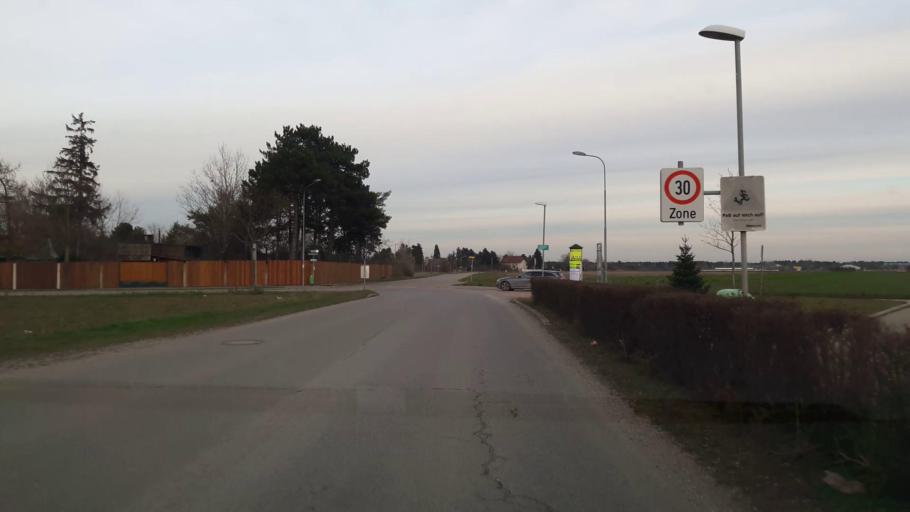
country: AT
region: Lower Austria
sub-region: Politischer Bezirk Ganserndorf
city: Parbasdorf
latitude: 48.3111
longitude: 16.5971
